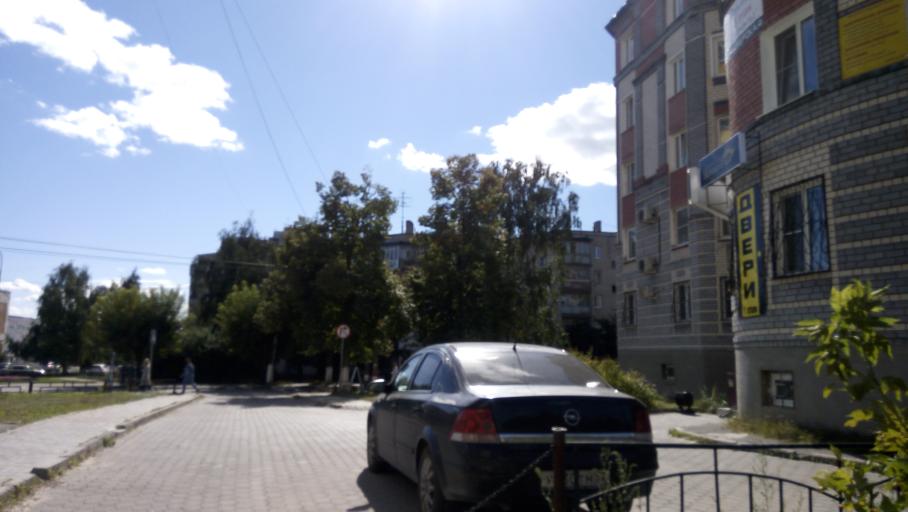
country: RU
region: Nizjnij Novgorod
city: Bor
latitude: 56.3569
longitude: 44.0624
